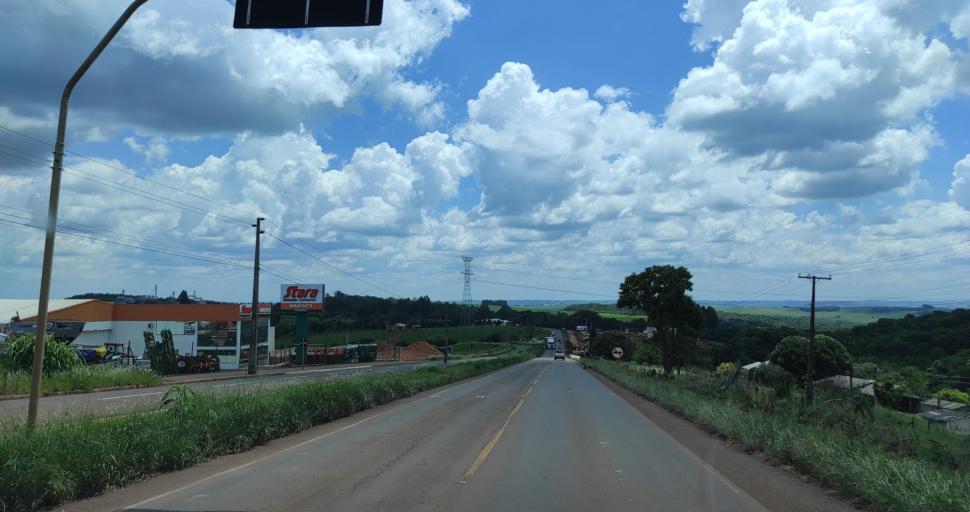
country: BR
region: Santa Catarina
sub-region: Xanxere
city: Xanxere
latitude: -26.8468
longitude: -52.4072
